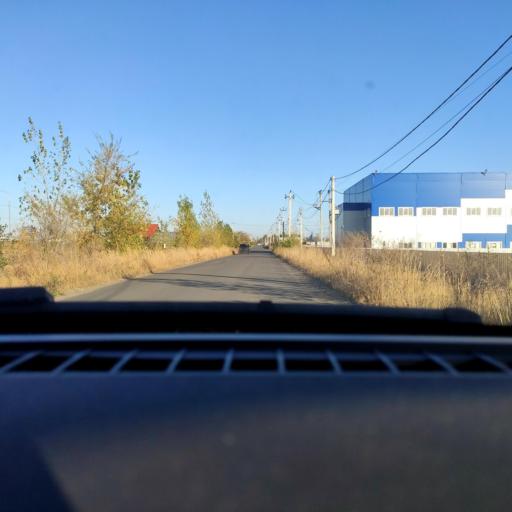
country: RU
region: Voronezj
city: Somovo
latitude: 51.6770
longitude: 39.3088
